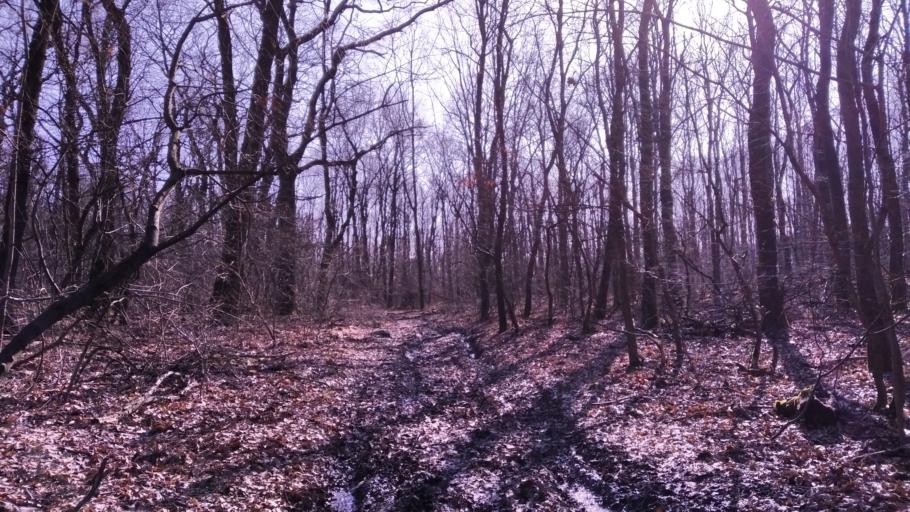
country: HU
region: Pest
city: Nagykovacsi
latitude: 47.6809
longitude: 19.0062
